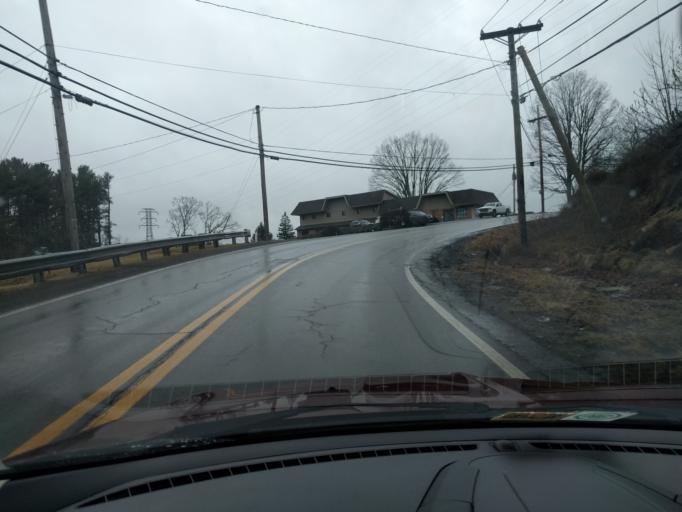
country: US
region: West Virginia
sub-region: Raleigh County
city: Beckley
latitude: 37.7920
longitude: -81.1783
